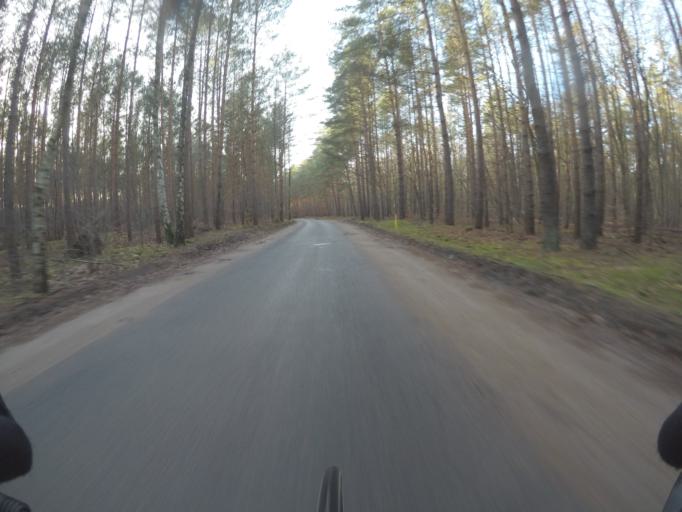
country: DE
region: Brandenburg
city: Birkenwerder
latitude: 52.6856
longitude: 13.3059
